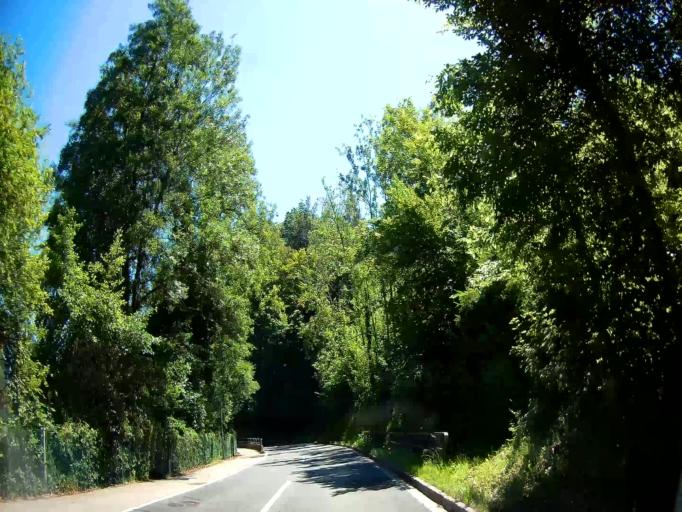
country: AT
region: Carinthia
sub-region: Politischer Bezirk Klagenfurt Land
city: Keutschach am See
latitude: 46.6098
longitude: 14.2124
